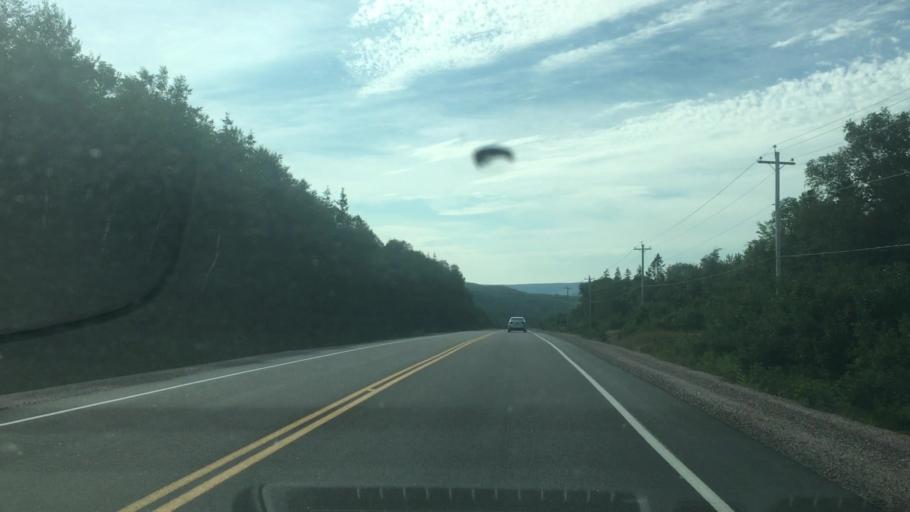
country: CA
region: Nova Scotia
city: Sydney Mines
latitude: 46.8551
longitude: -60.4435
